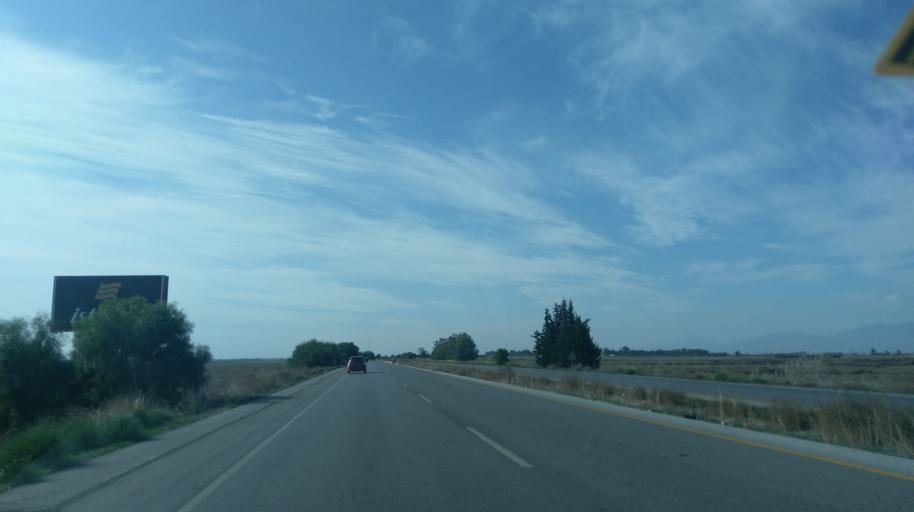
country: CY
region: Ammochostos
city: Lefkonoiko
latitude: 35.1787
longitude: 33.7458
